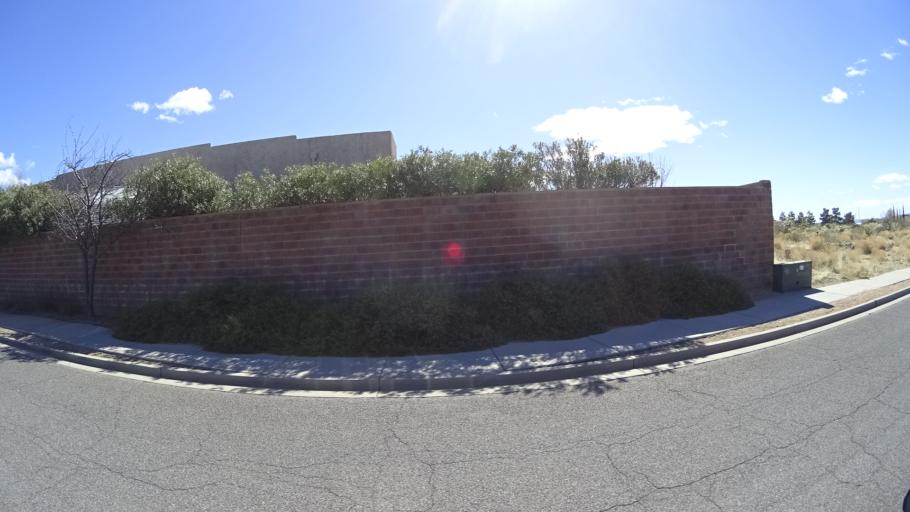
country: US
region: Arizona
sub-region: Mohave County
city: Kingman
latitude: 35.1922
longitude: -114.0097
